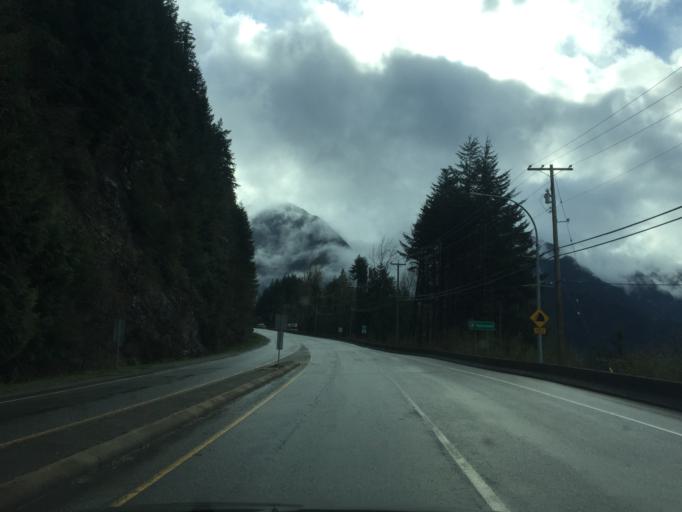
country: CA
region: British Columbia
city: Hope
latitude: 49.3712
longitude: -121.4455
